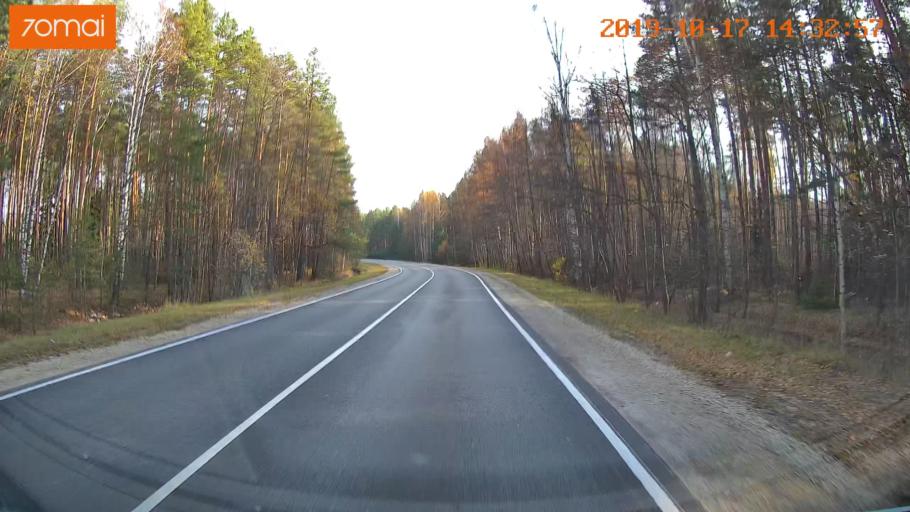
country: RU
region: Rjazan
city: Solotcha
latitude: 54.9261
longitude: 39.9888
